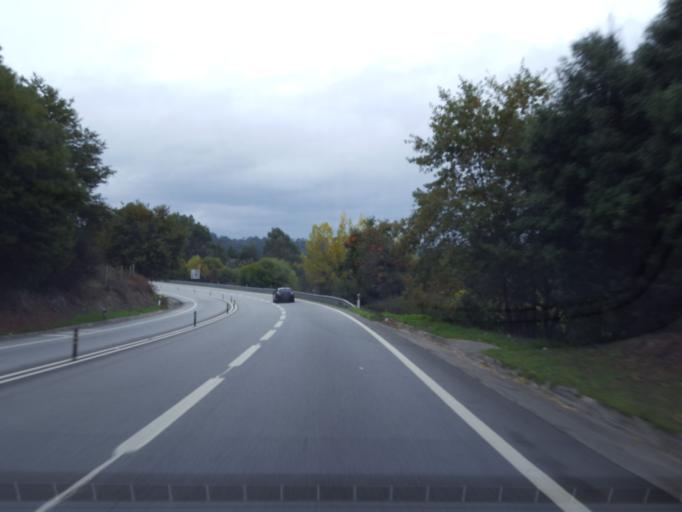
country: PT
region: Porto
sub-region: Lousada
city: Meinedo
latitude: 41.2315
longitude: -8.1995
